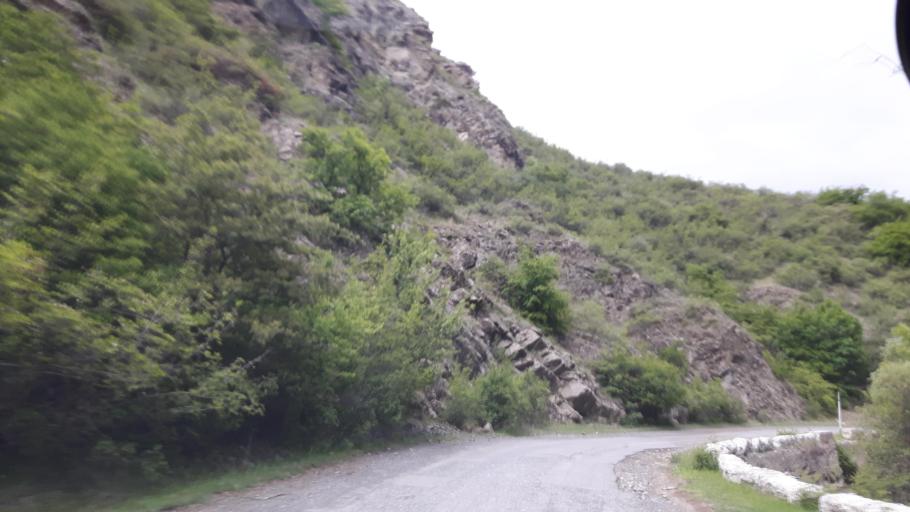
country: GE
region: Shida Kartli
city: Gori
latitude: 41.9008
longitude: 44.0657
